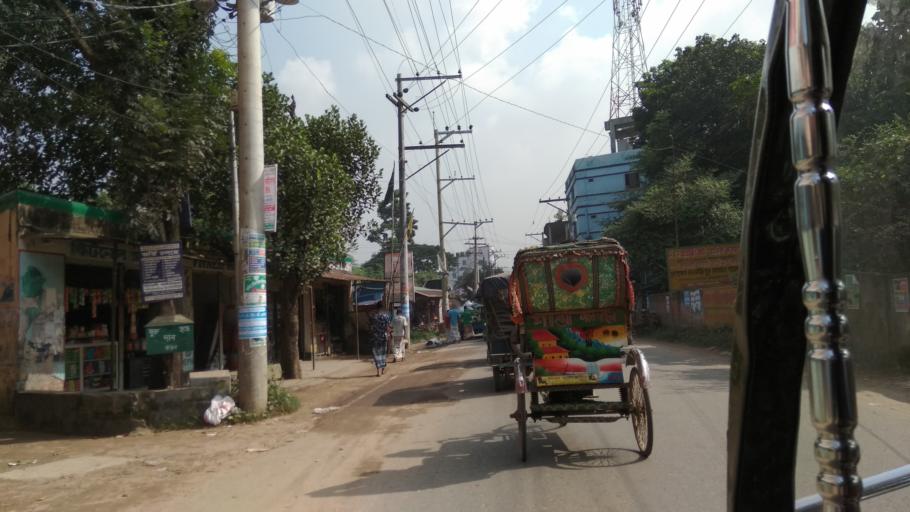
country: BD
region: Dhaka
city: Tungi
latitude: 23.9054
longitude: 90.2838
